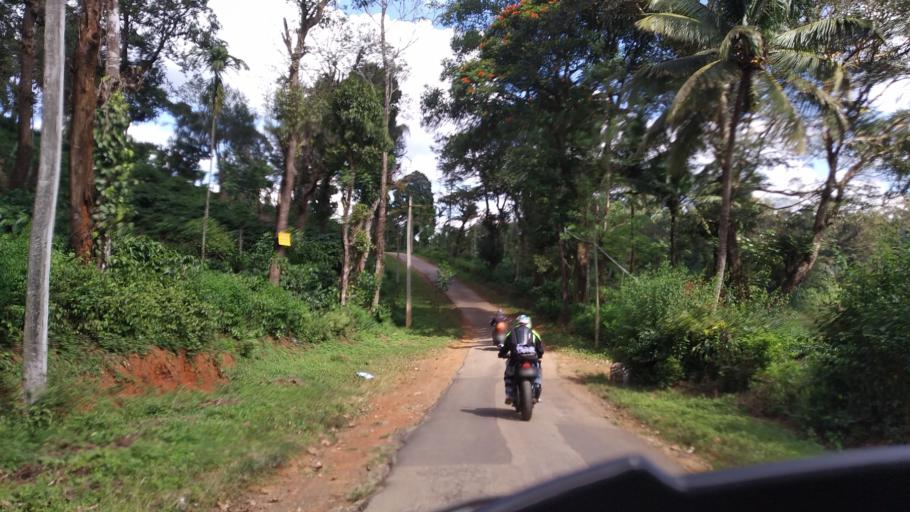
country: IN
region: Karnataka
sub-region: Kodagu
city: Ponnampet
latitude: 12.0347
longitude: 75.9129
